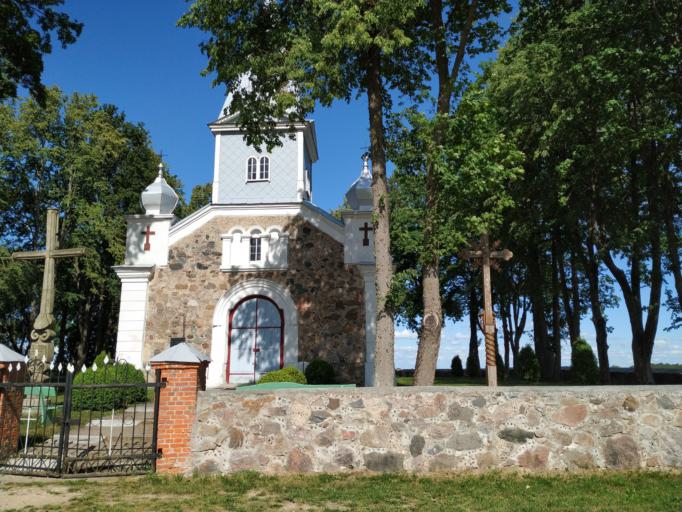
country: LT
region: Panevezys
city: Pasvalys
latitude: 56.1278
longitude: 24.3233
